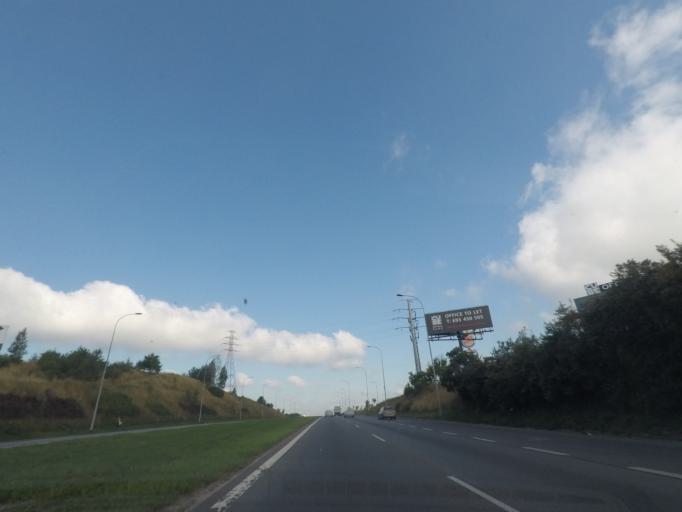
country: PL
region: Pomeranian Voivodeship
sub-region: Powiat gdanski
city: Kowale
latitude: 54.3381
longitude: 18.5556
